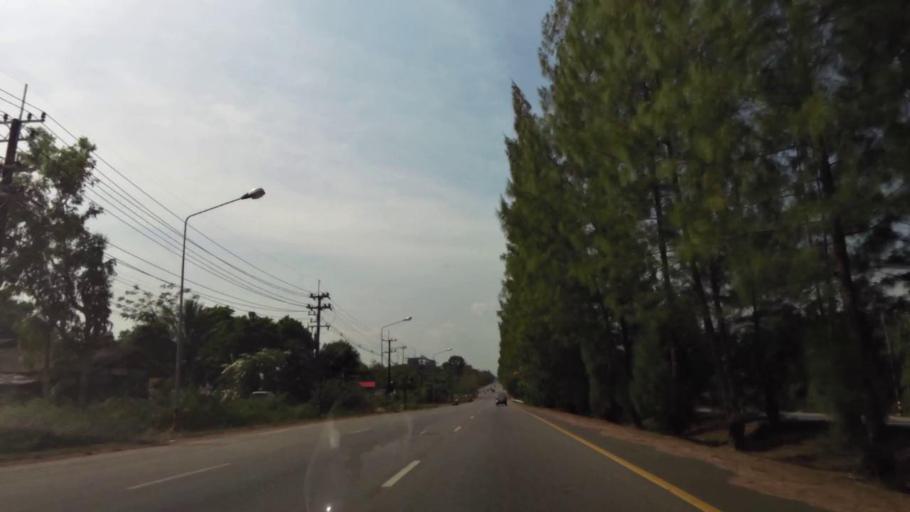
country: TH
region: Chanthaburi
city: Chanthaburi
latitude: 12.6639
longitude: 102.1145
